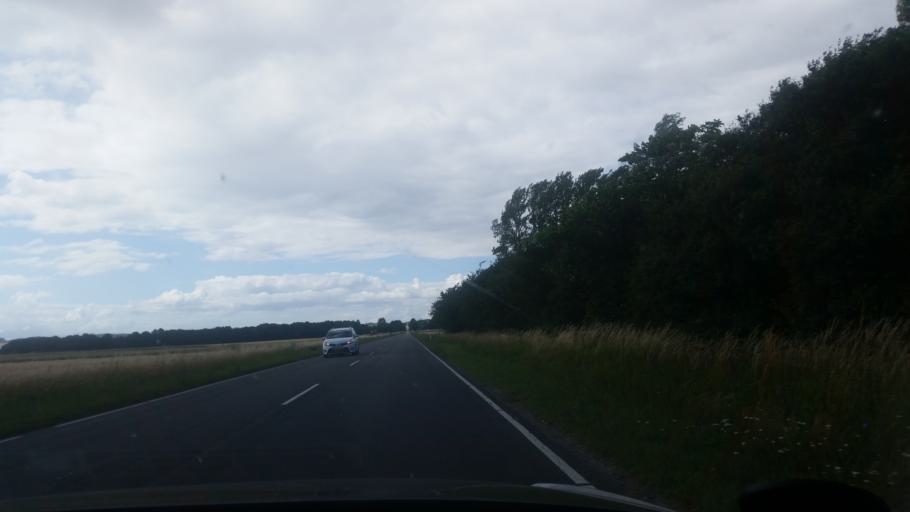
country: DK
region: Zealand
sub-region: Odsherred Kommune
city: Asnaes
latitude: 55.7708
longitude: 11.4918
